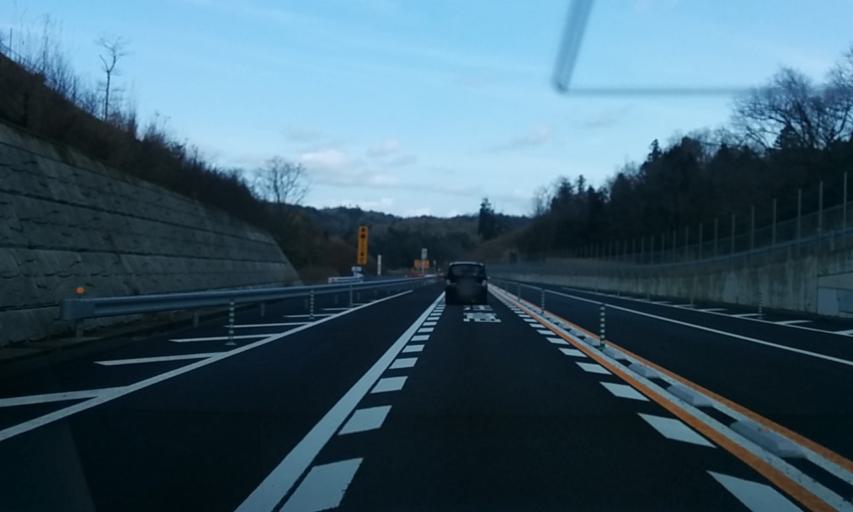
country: JP
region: Kyoto
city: Miyazu
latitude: 35.5721
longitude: 135.1212
